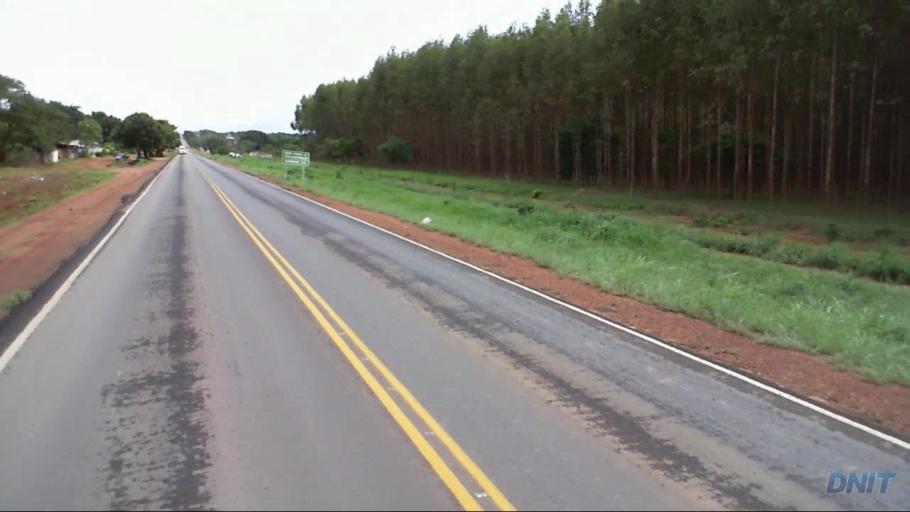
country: BR
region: Goias
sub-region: Padre Bernardo
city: Padre Bernardo
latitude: -15.2683
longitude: -48.2634
